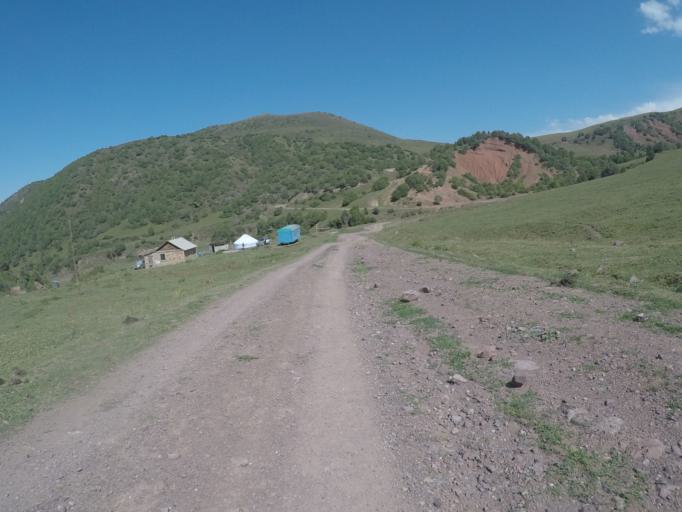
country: KG
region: Chuy
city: Bishkek
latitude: 42.6464
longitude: 74.5737
